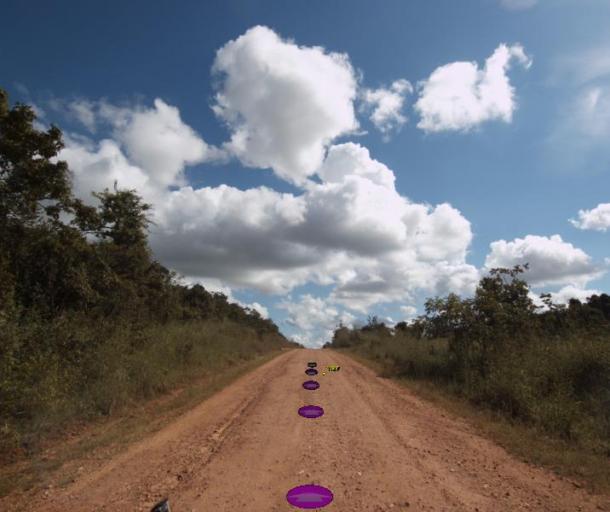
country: BR
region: Goias
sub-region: Jaragua
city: Jaragua
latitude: -15.8205
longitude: -49.1962
